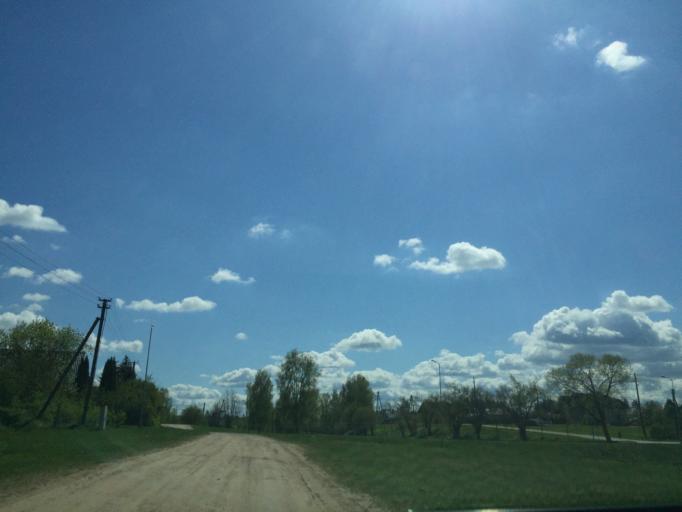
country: LV
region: Baldone
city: Baldone
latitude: 56.7394
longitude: 24.3762
